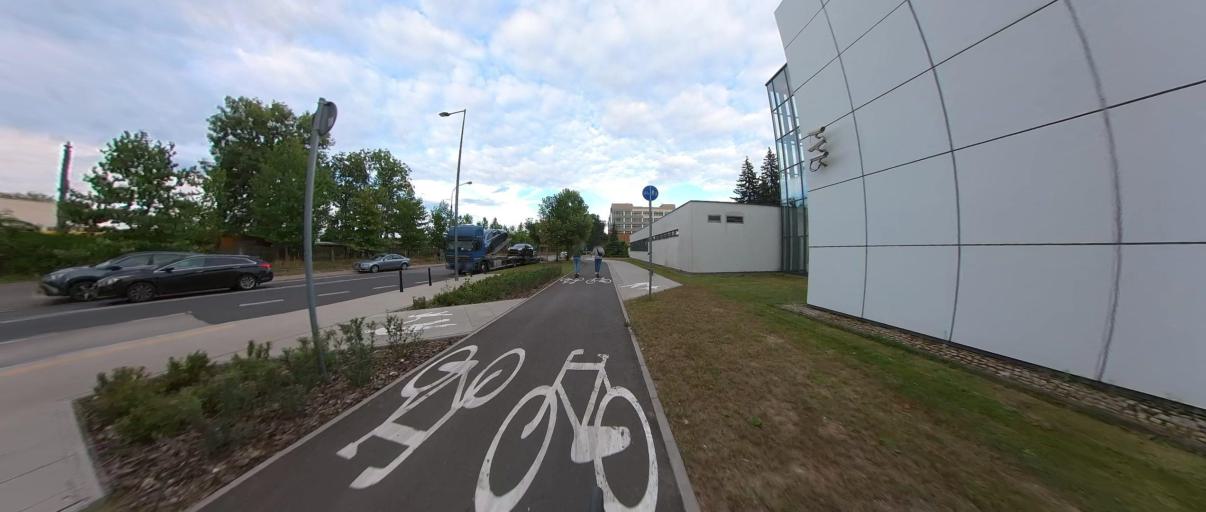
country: PL
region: Masovian Voivodeship
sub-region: Warszawa
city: Ochota
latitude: 52.1868
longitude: 20.9958
